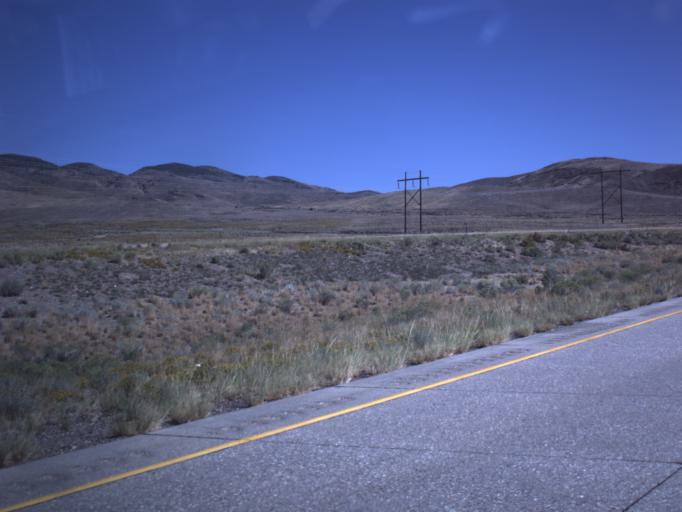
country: US
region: Utah
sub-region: Sevier County
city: Monroe
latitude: 38.6571
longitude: -112.2019
